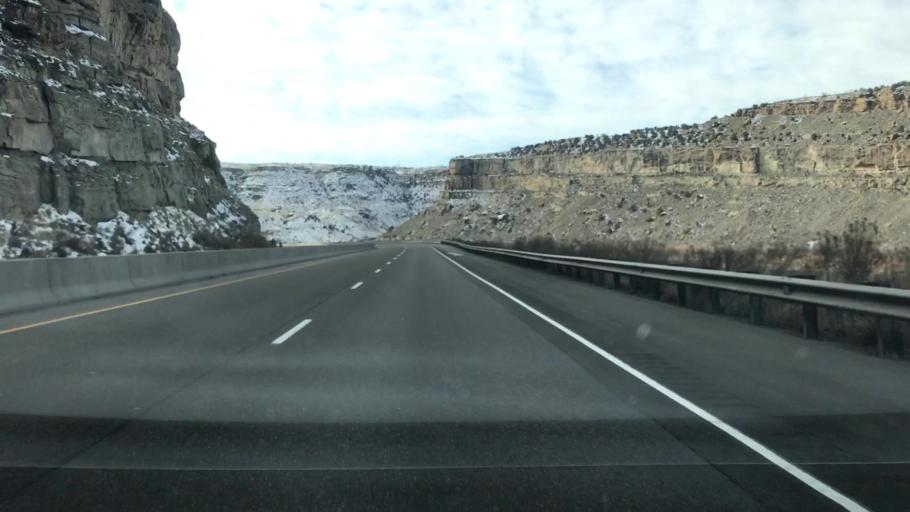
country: US
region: Colorado
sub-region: Mesa County
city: Palisade
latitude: 39.2620
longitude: -108.2574
